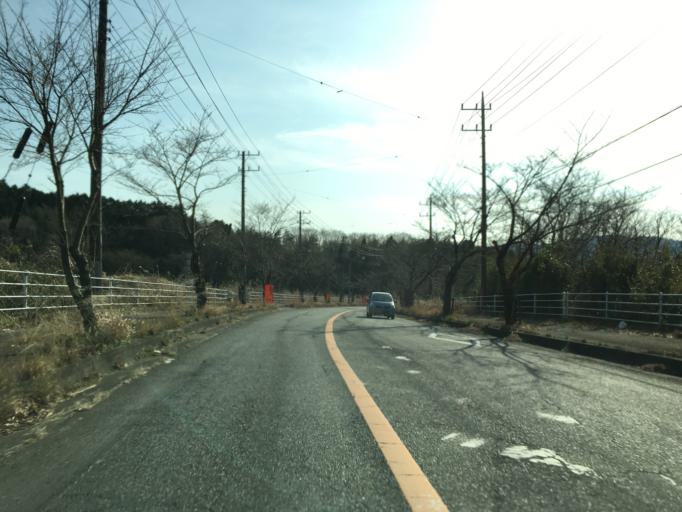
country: JP
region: Ibaraki
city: Takahagi
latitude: 36.7516
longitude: 140.7057
